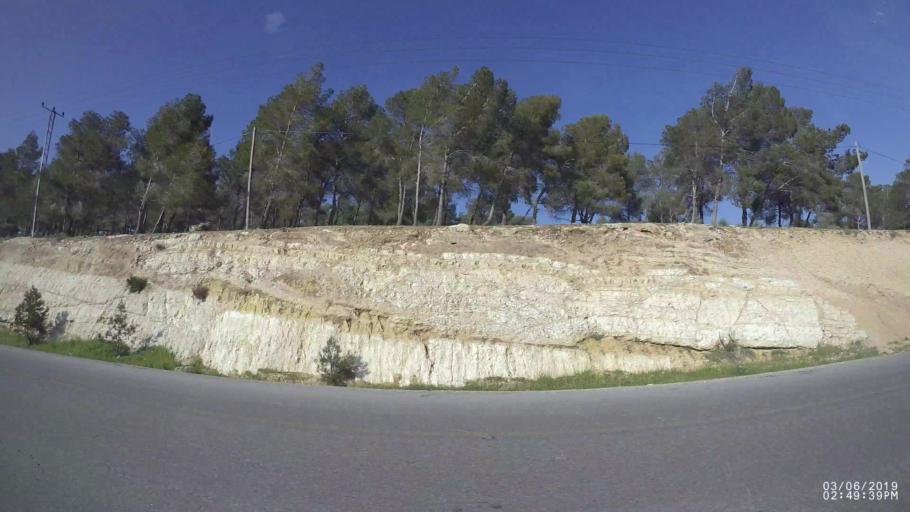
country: JO
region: Amman
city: Amman
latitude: 32.0210
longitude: 35.9429
